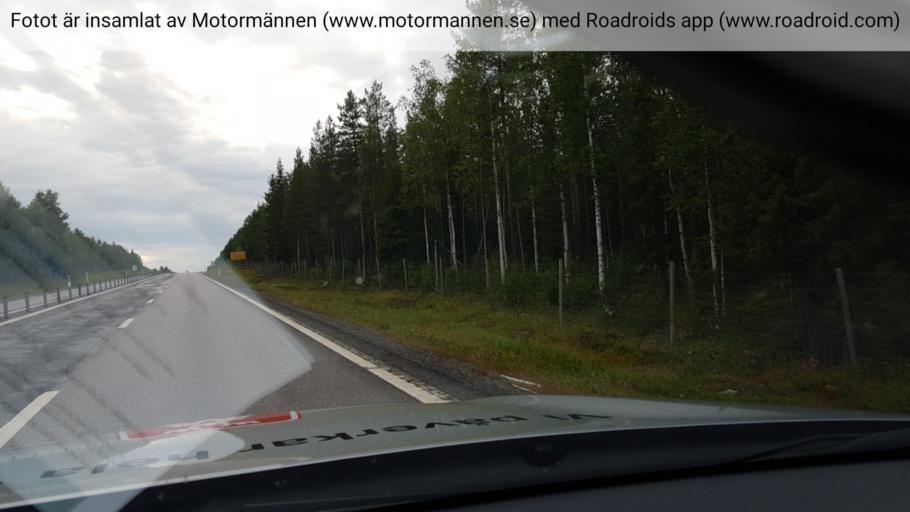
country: SE
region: Norrbotten
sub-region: Lulea Kommun
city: Ranea
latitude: 65.8728
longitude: 22.4223
